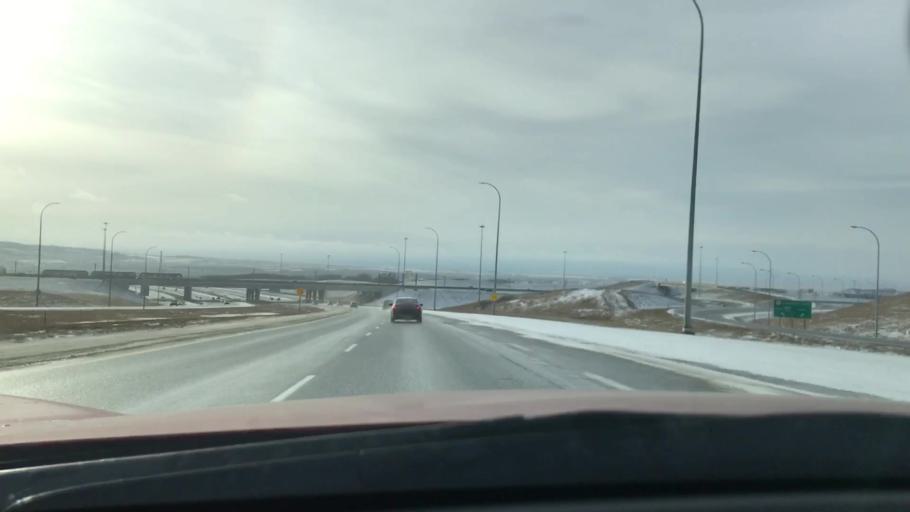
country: CA
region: Alberta
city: Calgary
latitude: 51.1351
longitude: -114.2227
